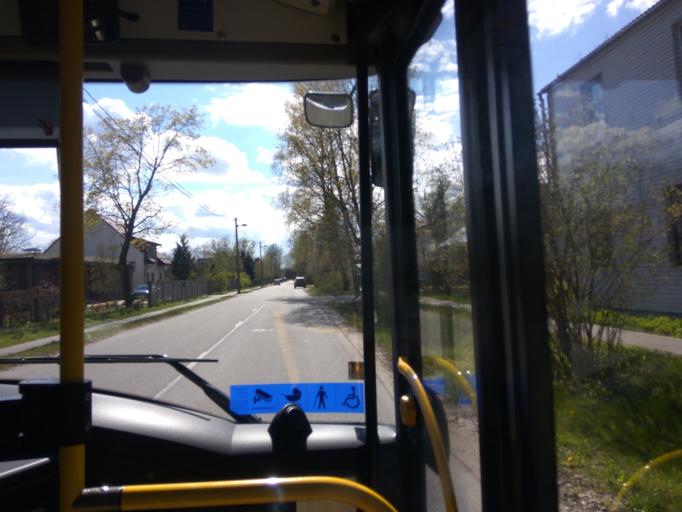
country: LV
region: Marupe
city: Marupe
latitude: 56.9317
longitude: 24.0245
